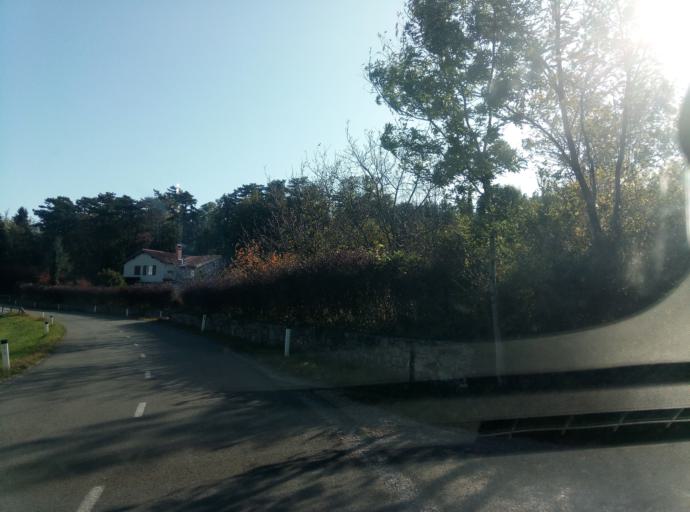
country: SI
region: Komen
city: Komen
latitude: 45.8205
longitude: 13.7465
